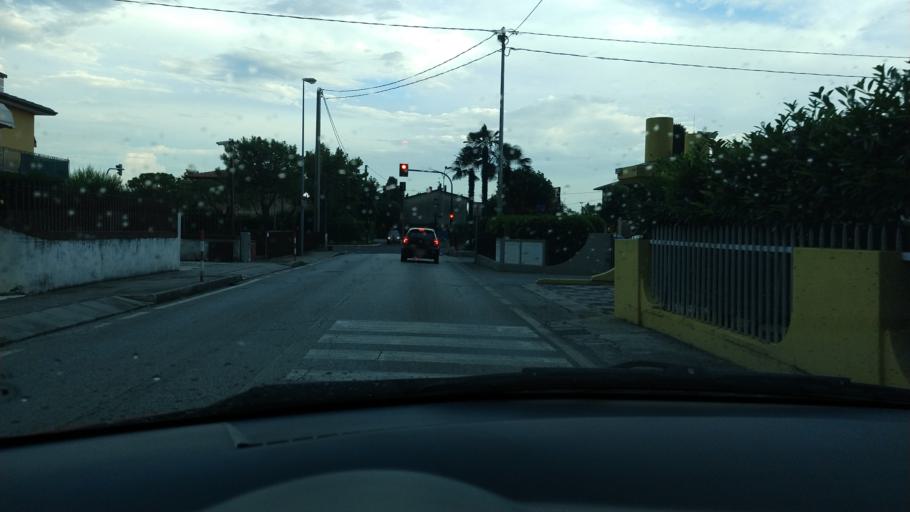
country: IT
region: Veneto
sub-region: Provincia di Vicenza
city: Fara Vicentino
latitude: 45.7378
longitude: 11.5388
